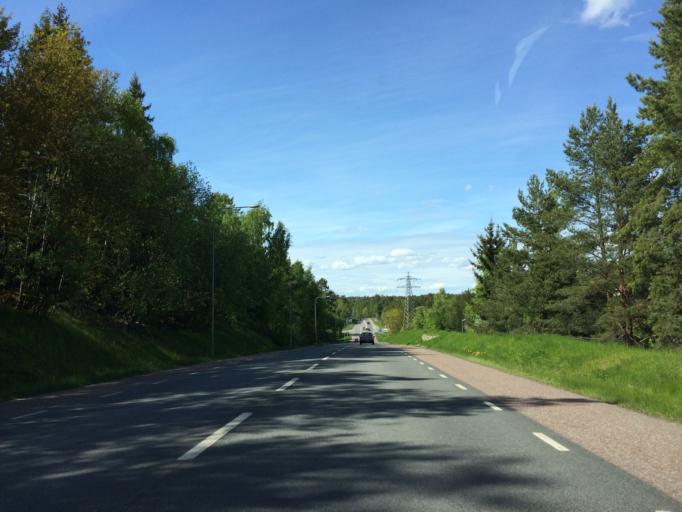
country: SE
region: Stockholm
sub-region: Sollentuna Kommun
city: Sollentuna
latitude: 59.4307
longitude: 17.9941
